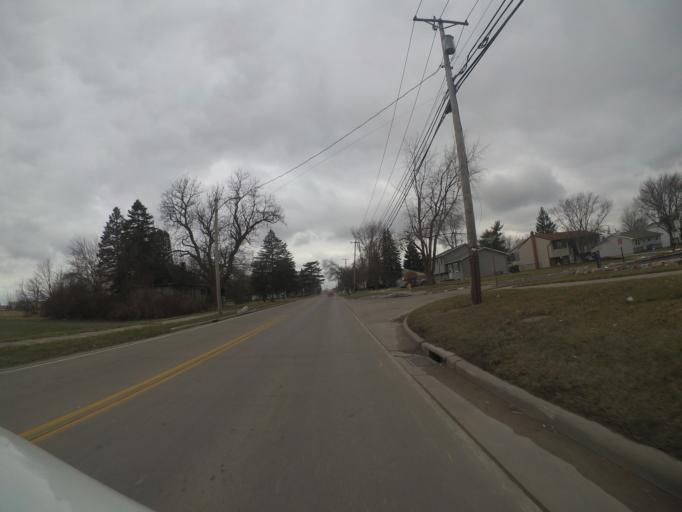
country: US
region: Ohio
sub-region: Wood County
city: Rossford
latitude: 41.6090
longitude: -83.5302
